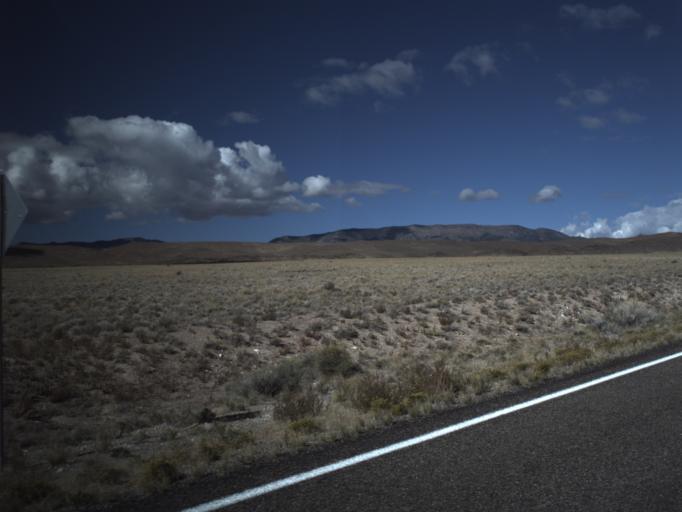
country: US
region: Utah
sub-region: Beaver County
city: Milford
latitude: 38.5813
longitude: -113.8088
